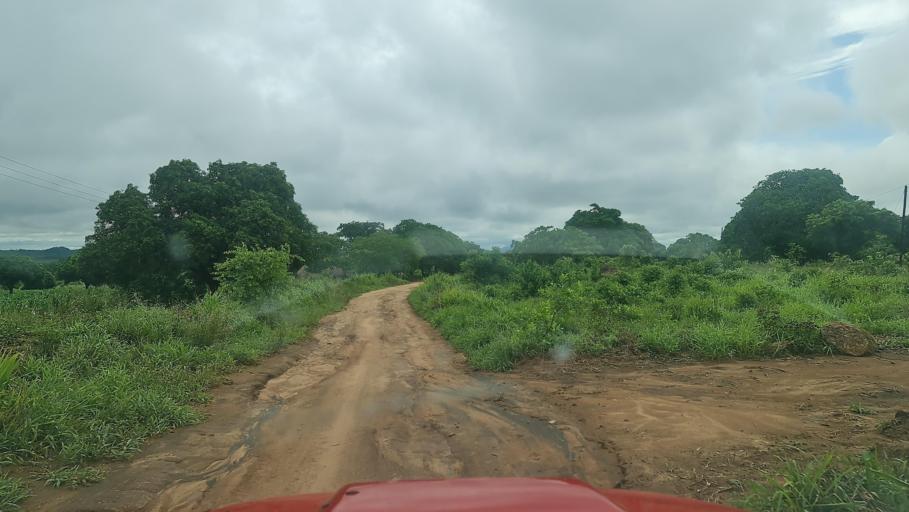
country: MW
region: Southern Region
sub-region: Nsanje District
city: Nsanje
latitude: -17.1808
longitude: 35.9106
